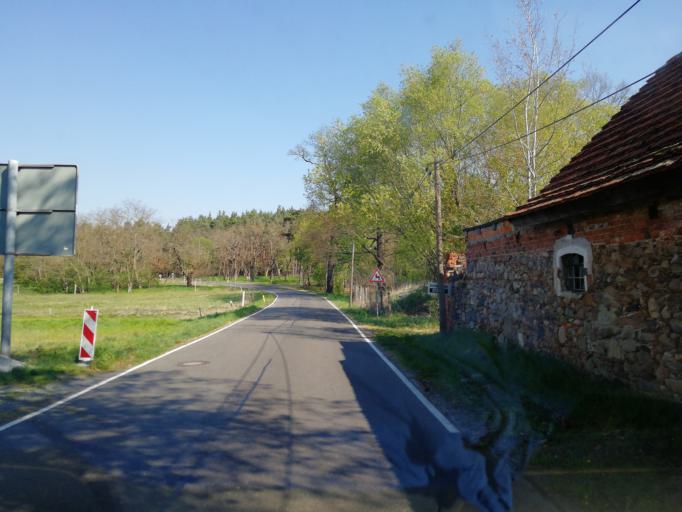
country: DE
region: Brandenburg
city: Bronkow
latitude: 51.7233
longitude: 13.8578
